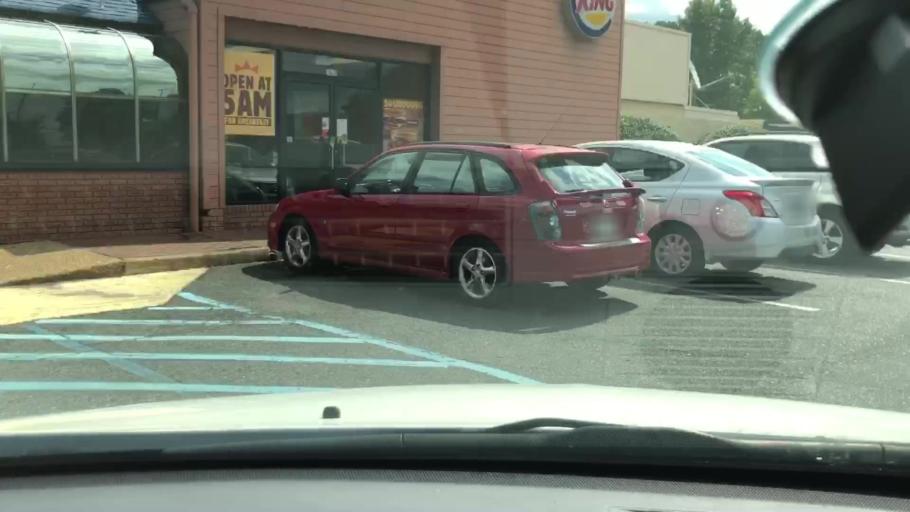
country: US
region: Virginia
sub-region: City of Chesapeake
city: Chesapeake
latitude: 36.7942
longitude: -76.2381
